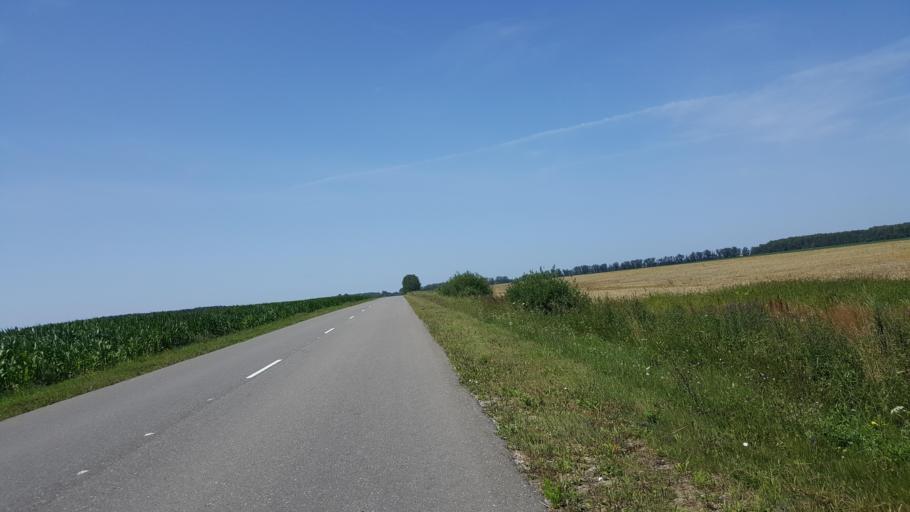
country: BY
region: Brest
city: Kamyanyets
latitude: 52.3767
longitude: 23.6153
